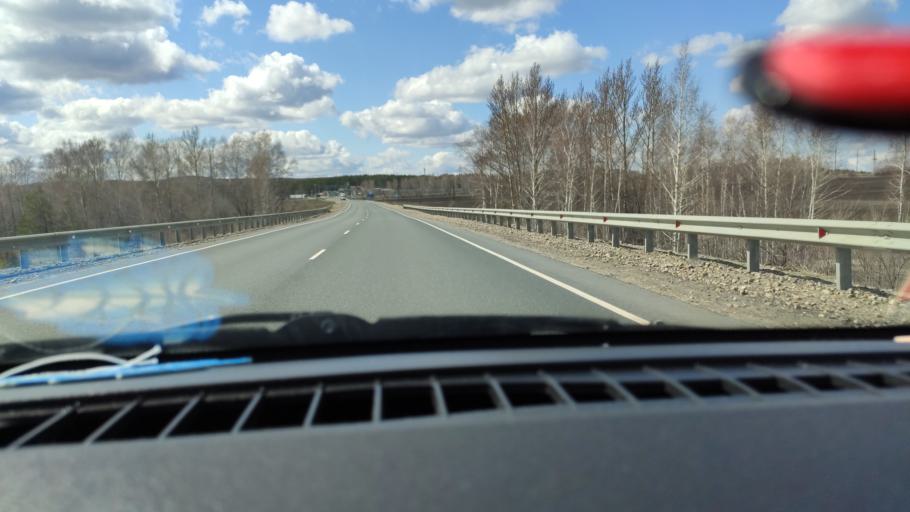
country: RU
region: Saratov
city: Khvalynsk
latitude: 52.5260
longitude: 48.0235
